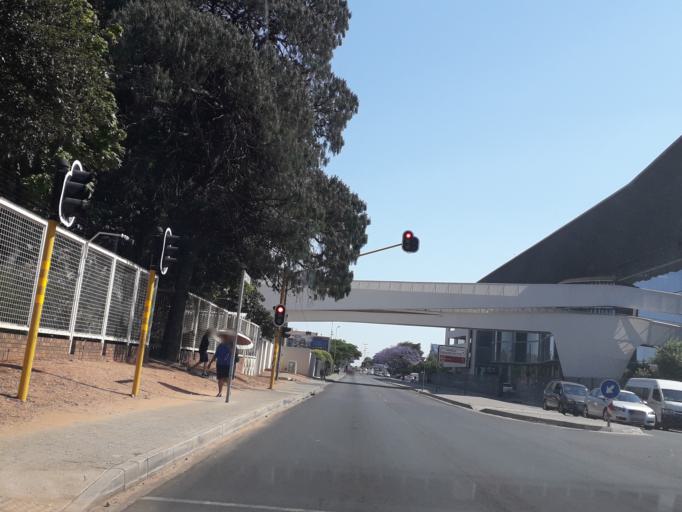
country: ZA
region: Gauteng
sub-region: City of Johannesburg Metropolitan Municipality
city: Johannesburg
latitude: -26.1023
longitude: 28.0023
